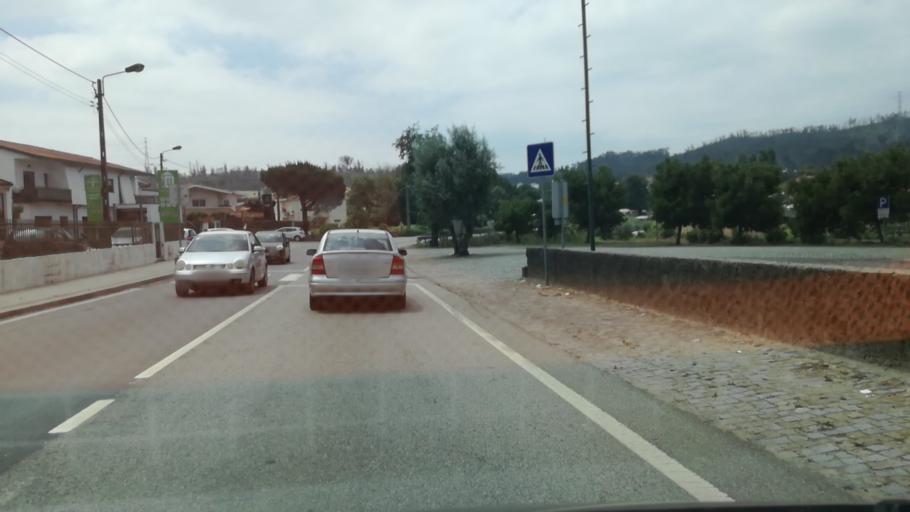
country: PT
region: Porto
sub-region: Trofa
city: Bougado
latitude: 41.3186
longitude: -8.5747
